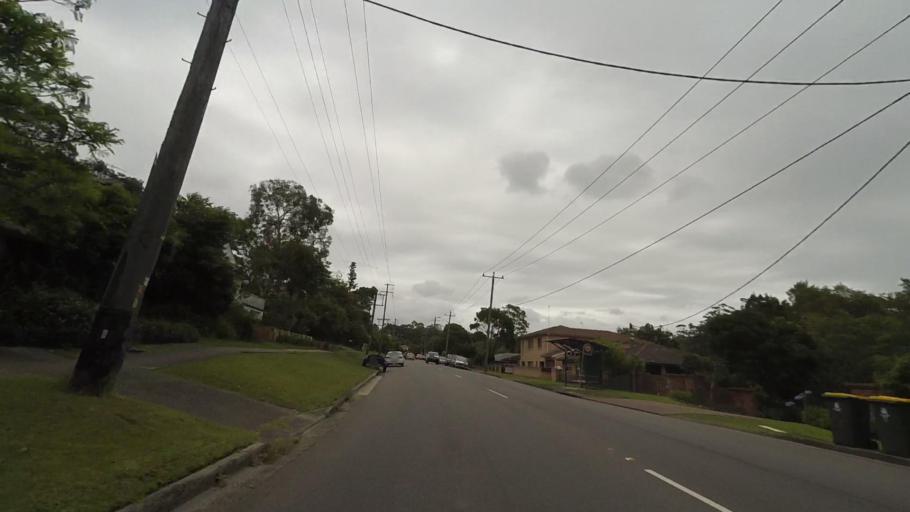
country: AU
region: New South Wales
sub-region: Lake Macquarie Shire
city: Kotara
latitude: -32.9435
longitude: 151.6950
